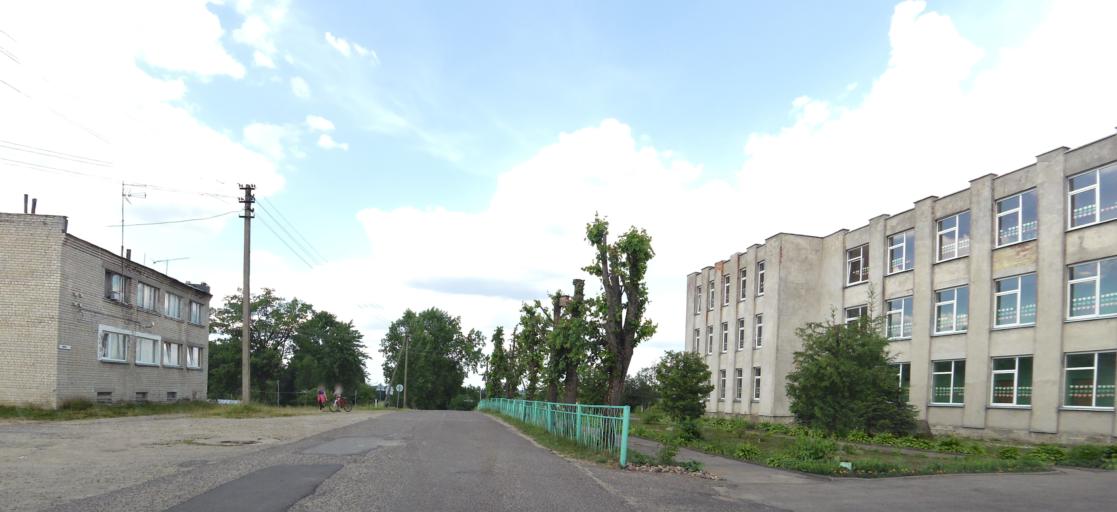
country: LT
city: Skaidiskes
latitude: 54.5366
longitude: 25.6514
